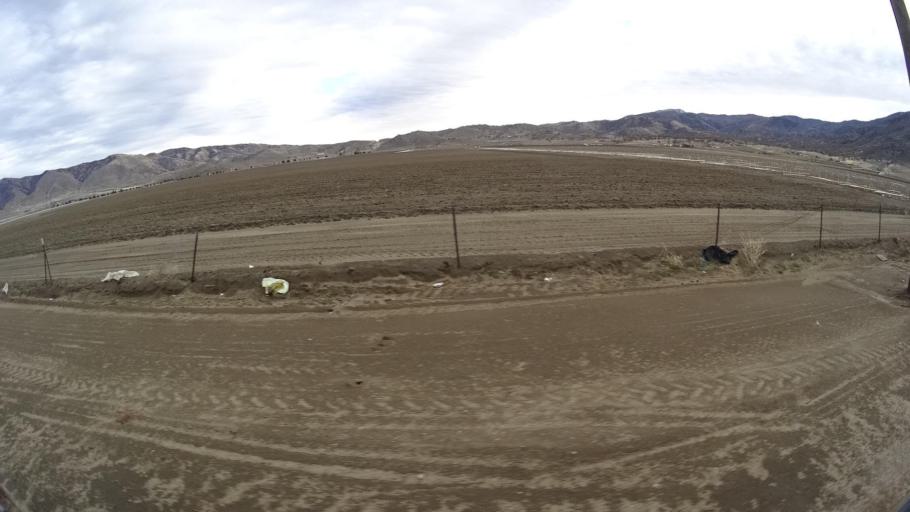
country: US
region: California
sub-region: Kern County
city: Stallion Springs
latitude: 35.1032
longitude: -118.6021
